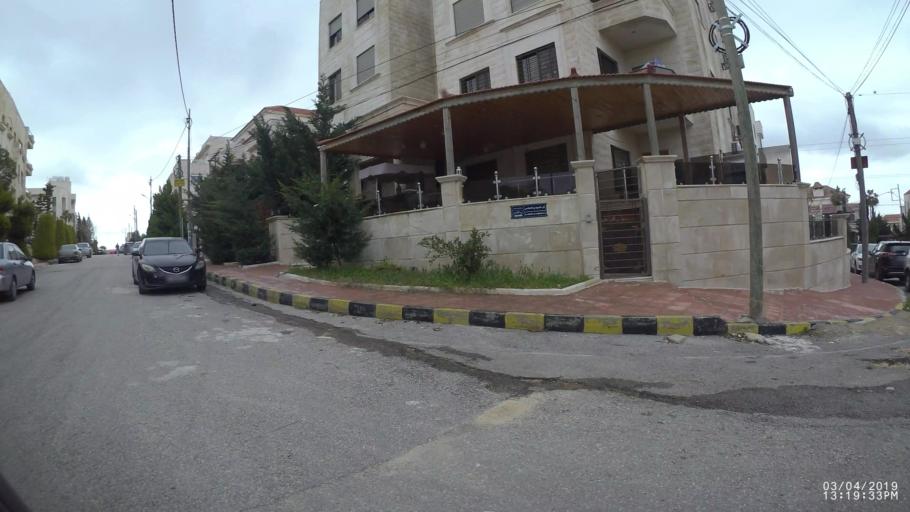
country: JO
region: Amman
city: Wadi as Sir
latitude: 31.9655
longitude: 35.8249
